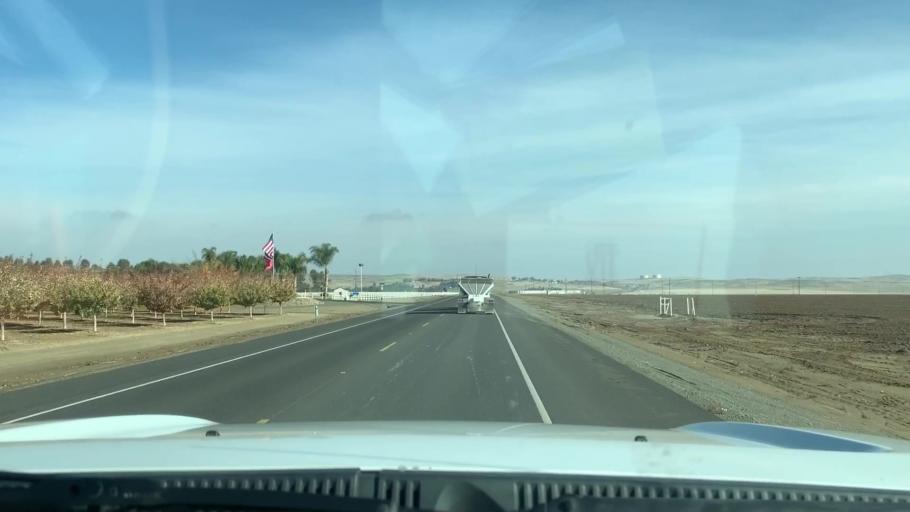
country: US
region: California
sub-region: Fresno County
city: Coalinga
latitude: 36.1903
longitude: -120.3422
